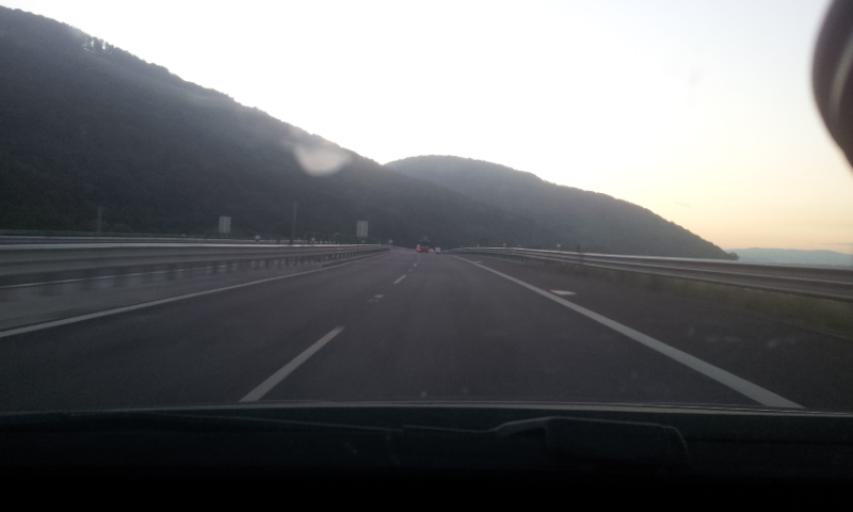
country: SK
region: Banskobystricky
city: Detva
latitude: 48.5411
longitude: 19.3445
